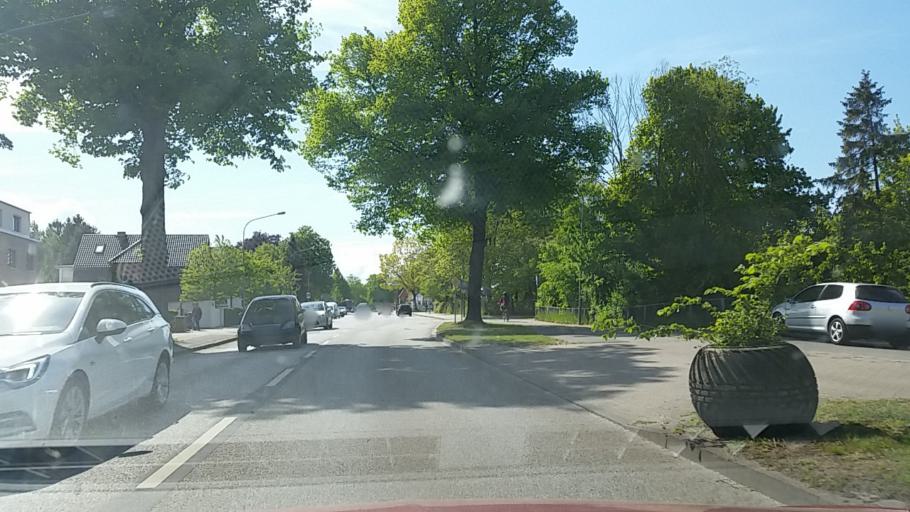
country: DE
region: Schleswig-Holstein
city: Stockelsdorf
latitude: 53.8502
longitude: 10.6461
